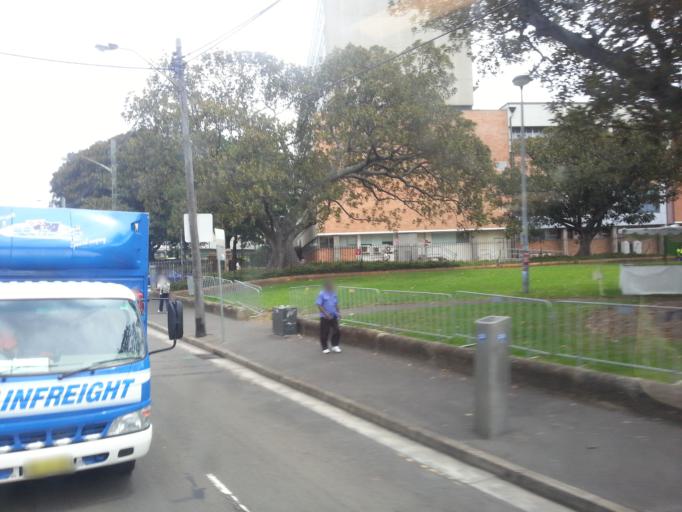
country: AU
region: New South Wales
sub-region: City of Sydney
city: Darlington
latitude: -33.8885
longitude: 151.1916
